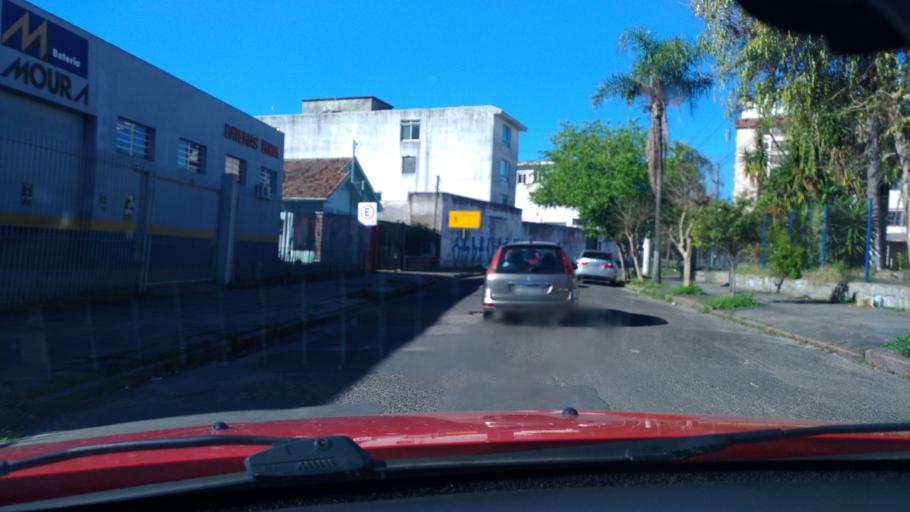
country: BR
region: Rio Grande do Sul
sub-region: Porto Alegre
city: Porto Alegre
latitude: -30.0101
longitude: -51.1708
